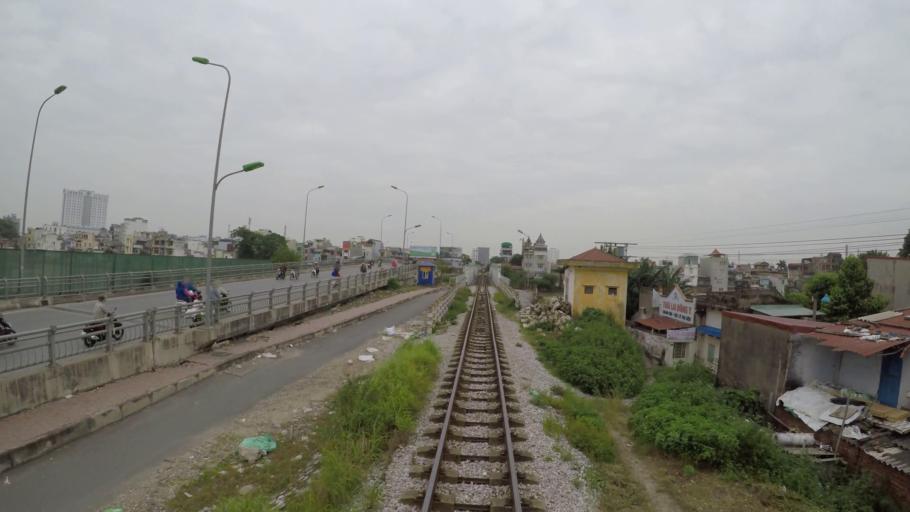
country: VN
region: Hai Phong
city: Haiphong
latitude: 20.8714
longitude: 106.6502
